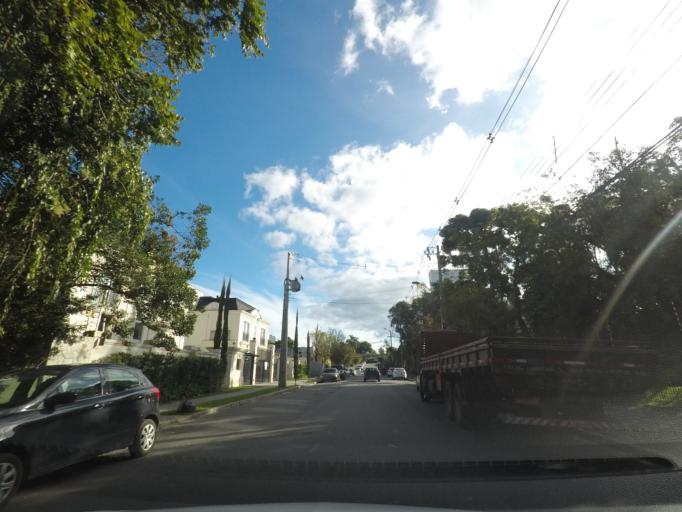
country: BR
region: Parana
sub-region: Curitiba
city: Curitiba
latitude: -25.4256
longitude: -49.2890
